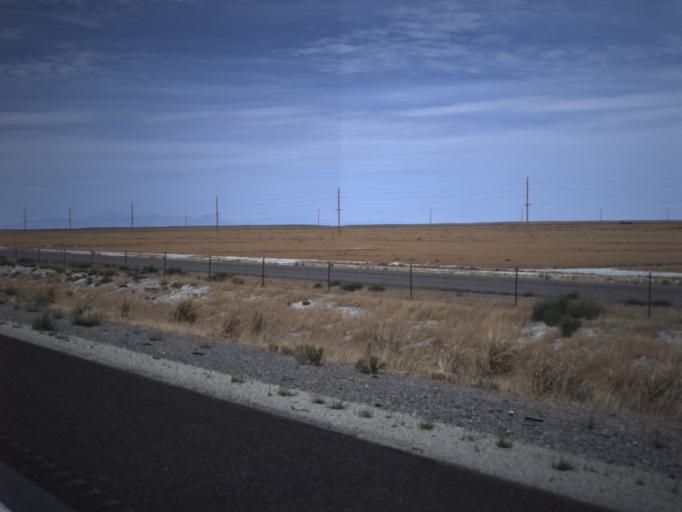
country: US
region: Utah
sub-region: Tooele County
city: Grantsville
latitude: 40.7266
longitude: -113.1945
